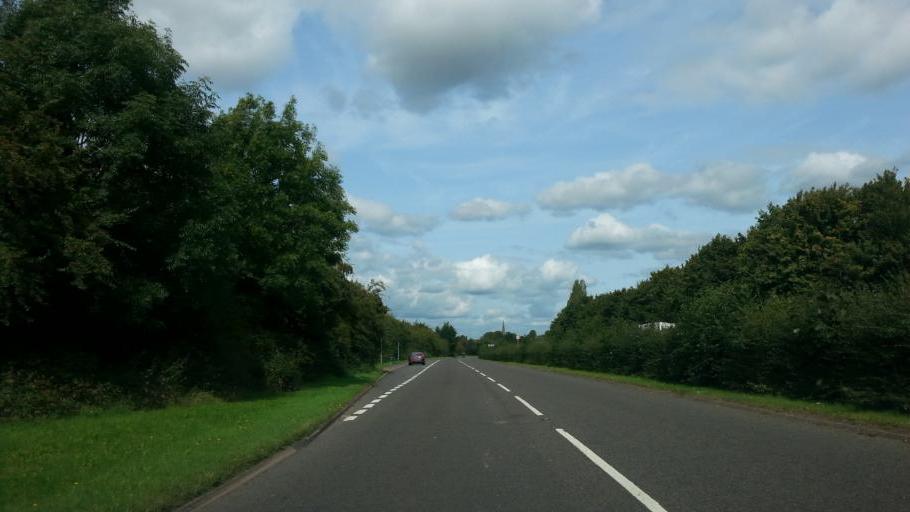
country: GB
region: England
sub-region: Leicestershire
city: Blaby
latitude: 52.5645
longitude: -1.1721
